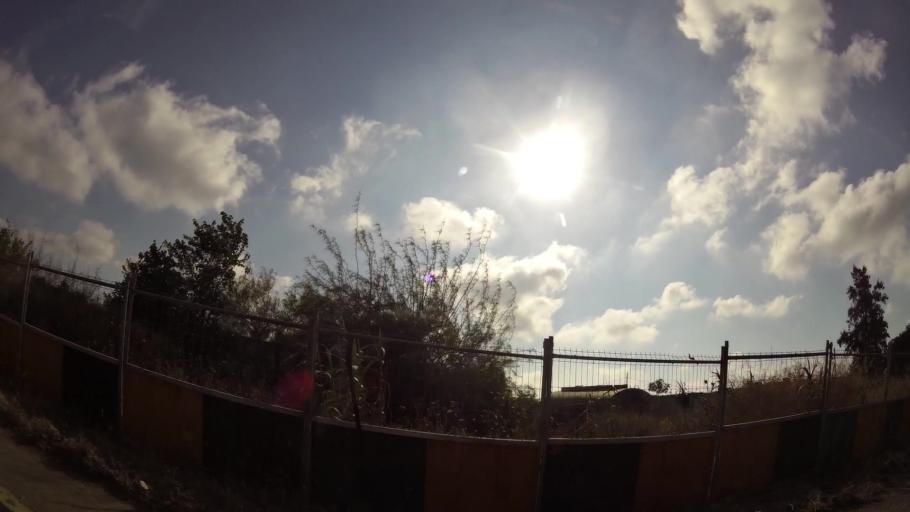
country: MA
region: Rabat-Sale-Zemmour-Zaer
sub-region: Rabat
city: Rabat
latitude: 33.9557
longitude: -6.8502
